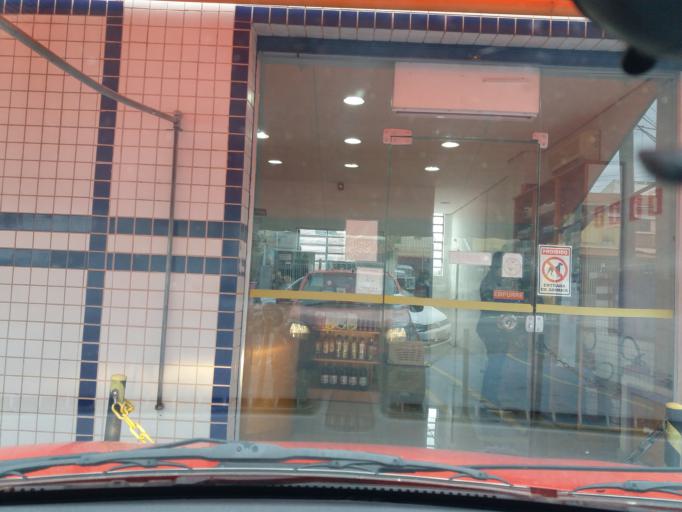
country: BR
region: Sao Paulo
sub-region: Osasco
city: Osasco
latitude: -23.5684
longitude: -46.7502
